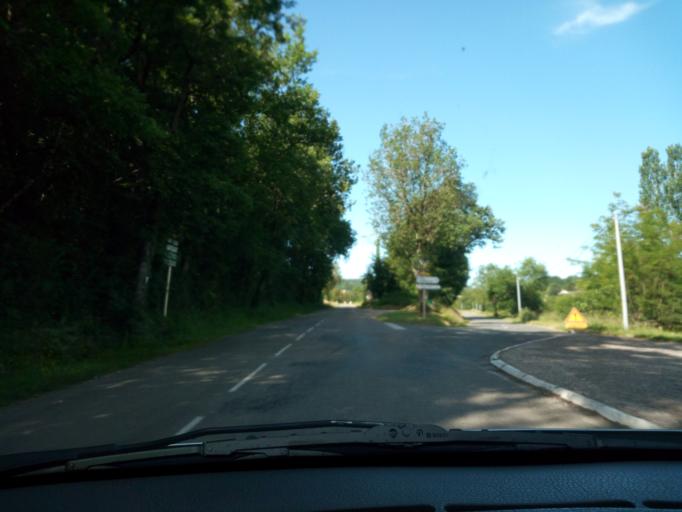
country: FR
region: Midi-Pyrenees
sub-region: Departement du Lot
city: Castelnau-Montratier
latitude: 44.2572
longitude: 1.3592
